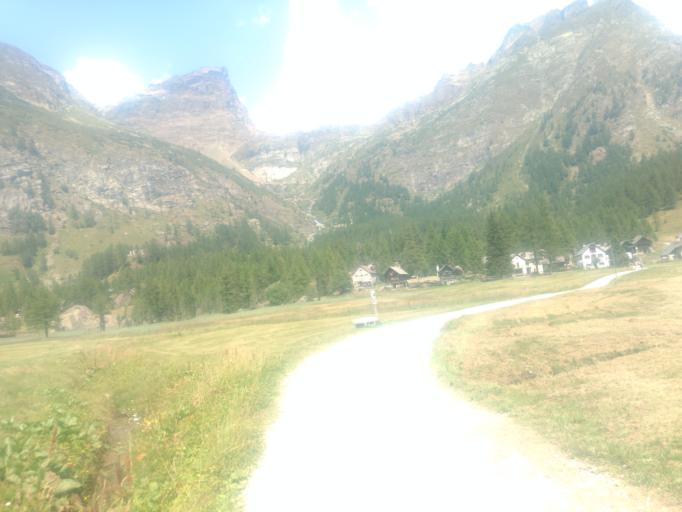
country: IT
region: Piedmont
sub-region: Provincia Verbano-Cusio-Ossola
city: Baceno
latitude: 46.3184
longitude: 8.2613
